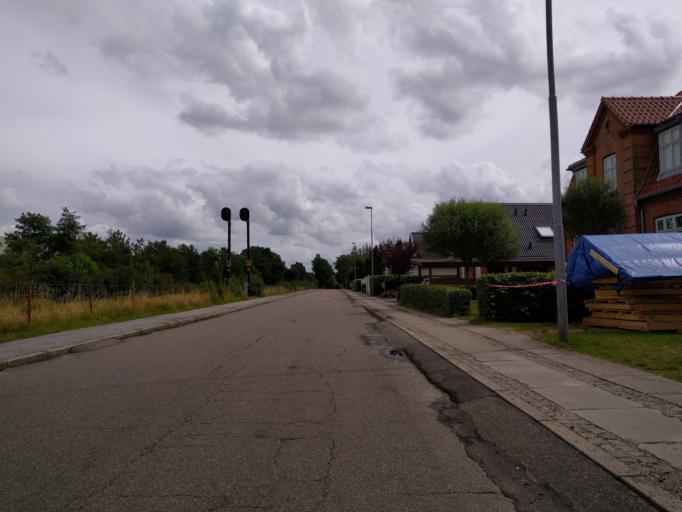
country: DK
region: Central Jutland
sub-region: Skanderborg Kommune
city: Ry
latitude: 56.0884
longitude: 9.7608
